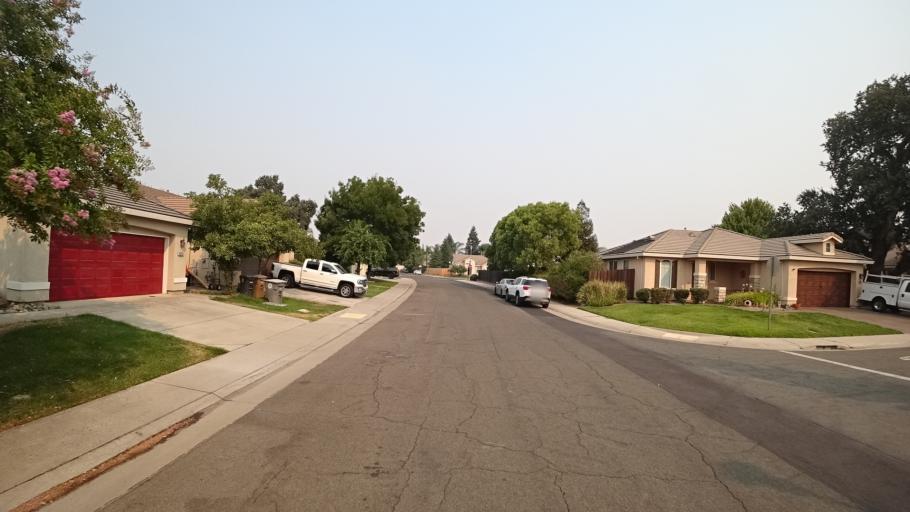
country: US
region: California
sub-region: Sacramento County
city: Laguna
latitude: 38.4032
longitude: -121.4476
